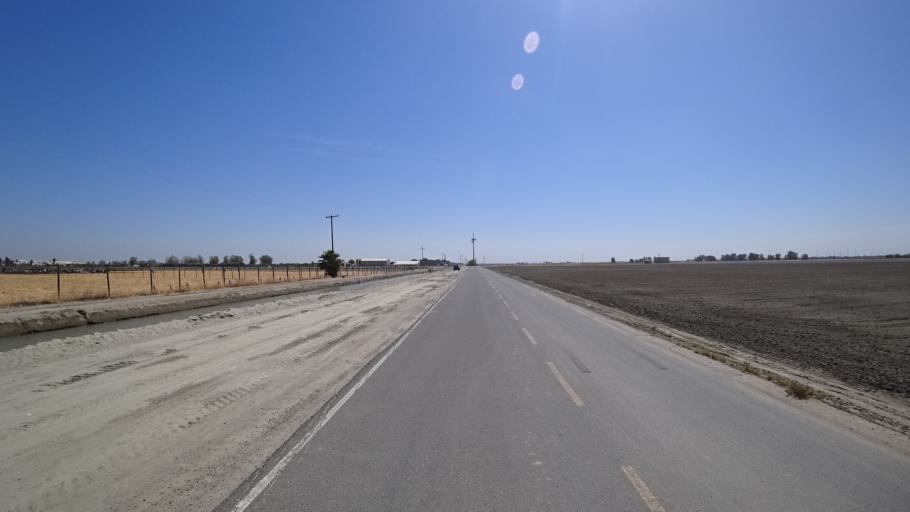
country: US
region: California
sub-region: Kings County
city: Corcoran
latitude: 36.0724
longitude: -119.5624
